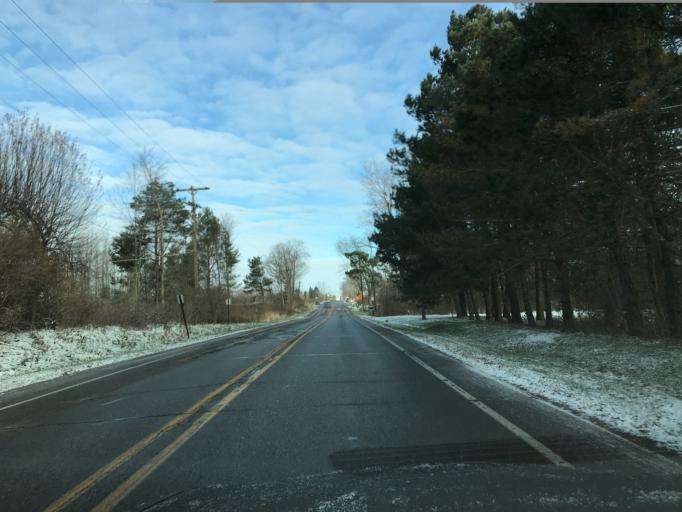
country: US
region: Michigan
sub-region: Eaton County
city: Dimondale
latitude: 42.6767
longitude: -84.6423
